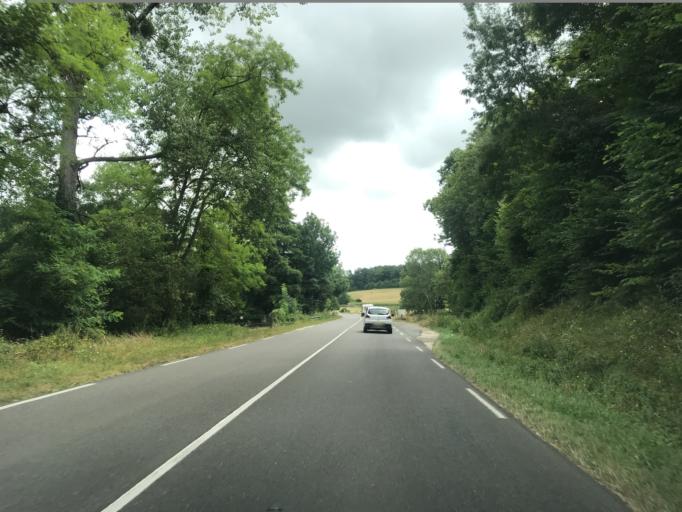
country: FR
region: Aquitaine
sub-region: Departement de la Dordogne
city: Mareuil
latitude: 45.4842
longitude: 0.3868
